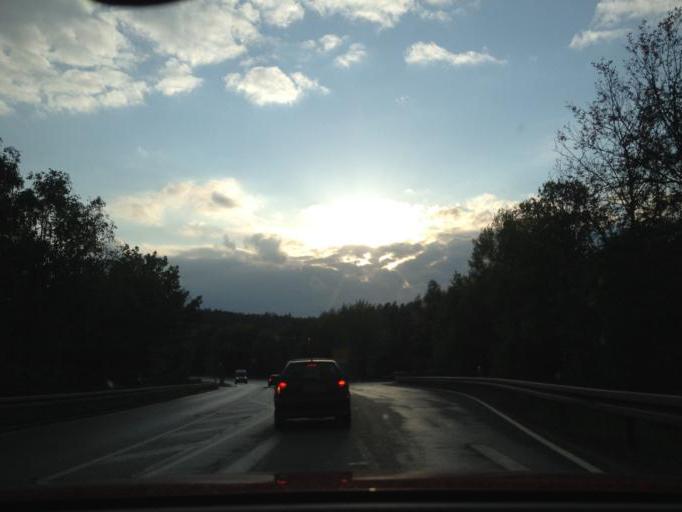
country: DE
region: Bavaria
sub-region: Upper Palatinate
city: Schirmitz
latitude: 49.6507
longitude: 12.1419
